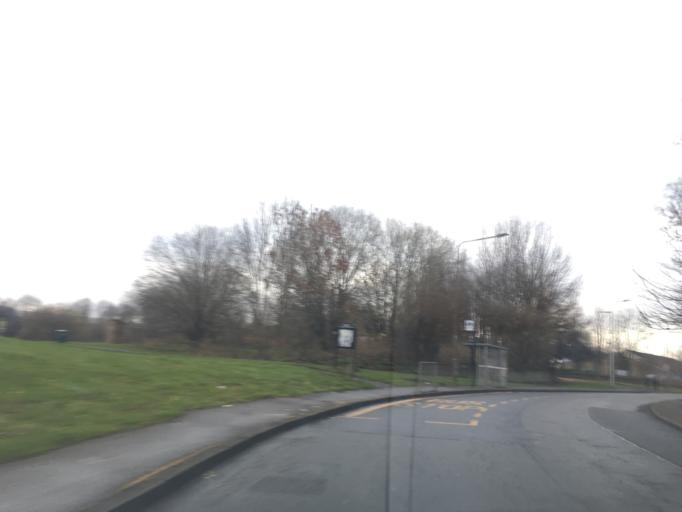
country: GB
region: Scotland
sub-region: Edinburgh
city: Colinton
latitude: 55.9206
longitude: -3.2709
